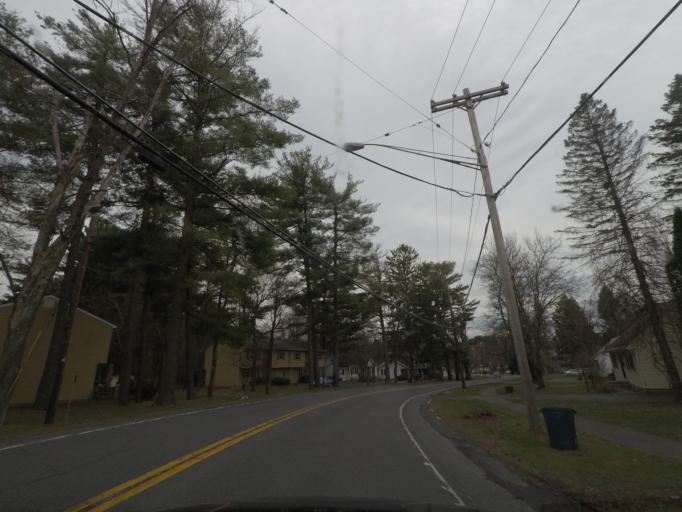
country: US
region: New York
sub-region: Albany County
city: Delmar
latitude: 42.6171
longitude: -73.8197
